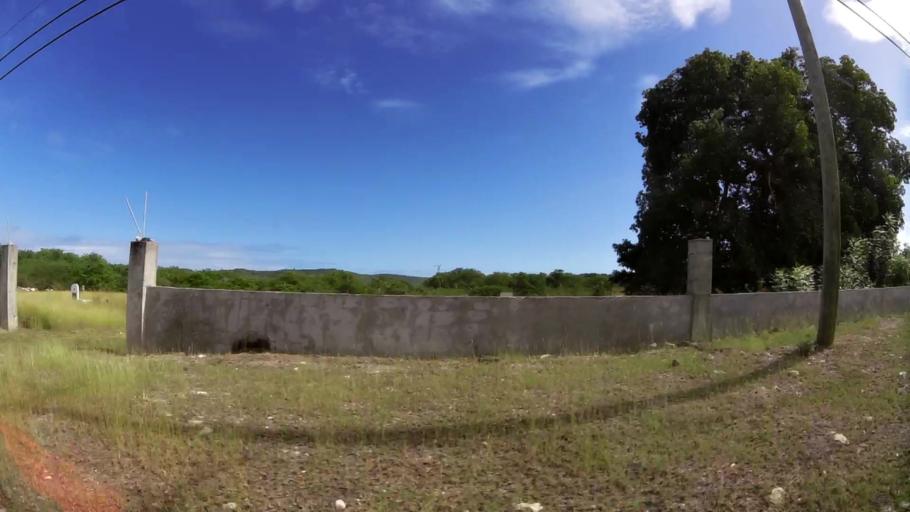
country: AG
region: Saint Paul
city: Falmouth
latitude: 17.0396
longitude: -61.7511
